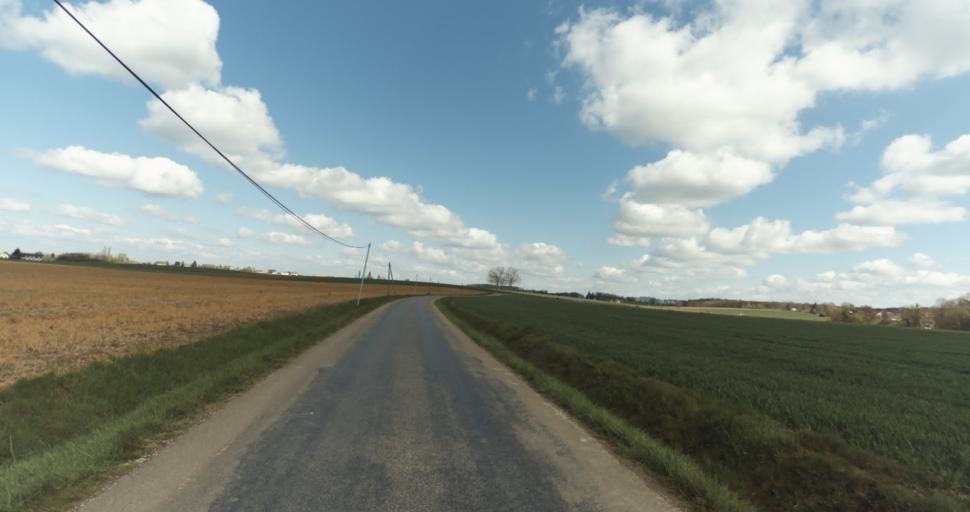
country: FR
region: Bourgogne
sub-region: Departement de la Cote-d'Or
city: Auxonne
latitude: 47.2041
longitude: 5.4236
